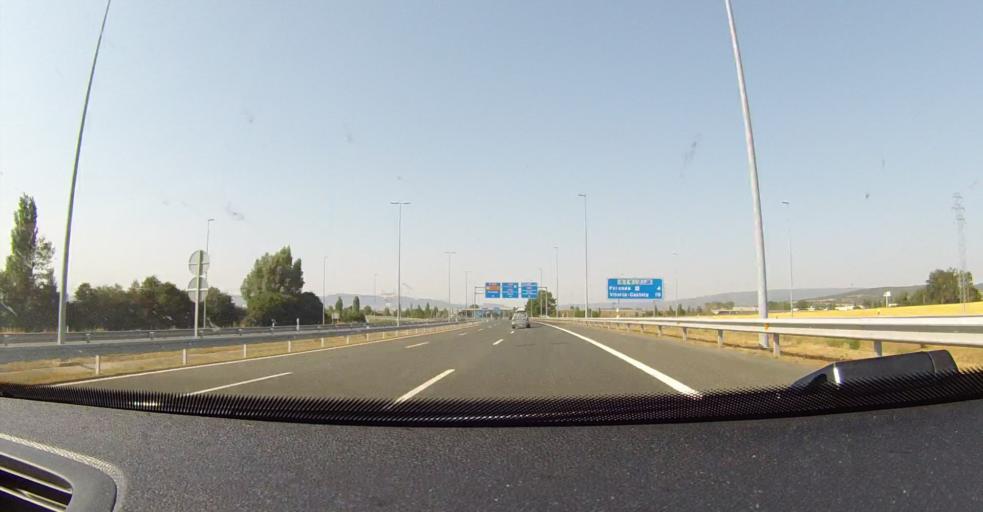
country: ES
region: Basque Country
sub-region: Provincia de Alava
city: Gasteiz / Vitoria
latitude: 42.9128
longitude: -2.7009
